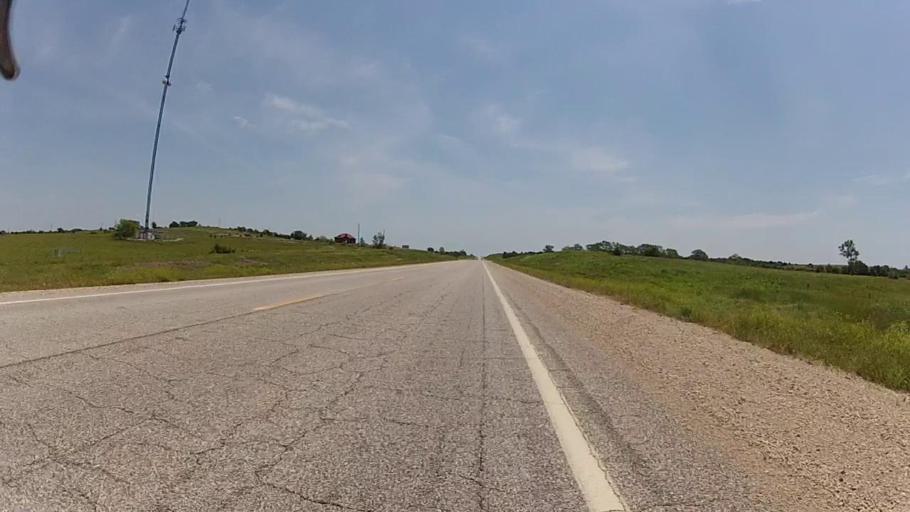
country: US
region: Kansas
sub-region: Chautauqua County
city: Sedan
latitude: 37.1132
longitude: -96.4557
